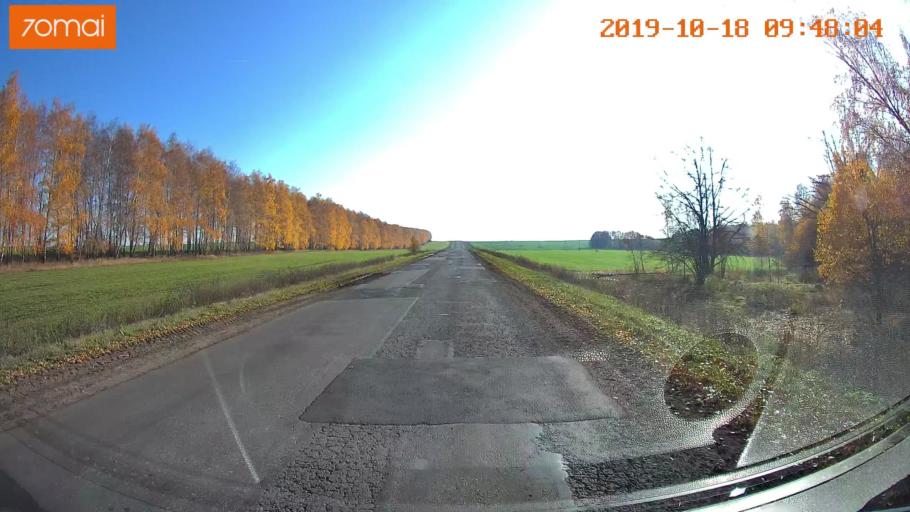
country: RU
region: Tula
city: Kazachka
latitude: 53.3195
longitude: 38.2413
